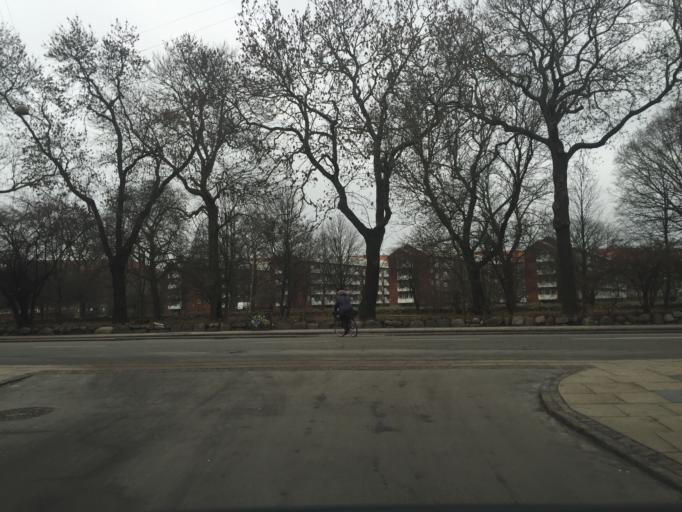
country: DK
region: Capital Region
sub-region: Kobenhavn
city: Christianshavn
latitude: 55.6611
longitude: 12.6207
